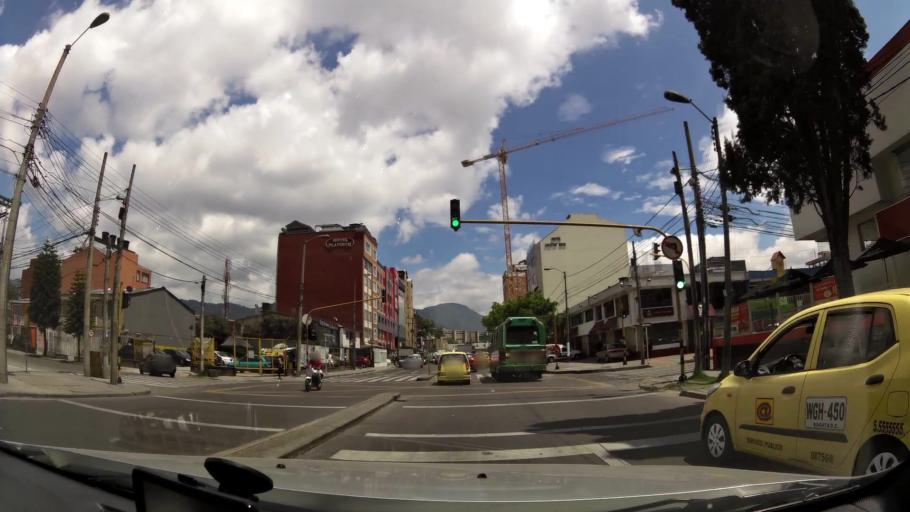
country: CO
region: Bogota D.C.
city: Bogota
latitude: 4.6323
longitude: -74.0938
